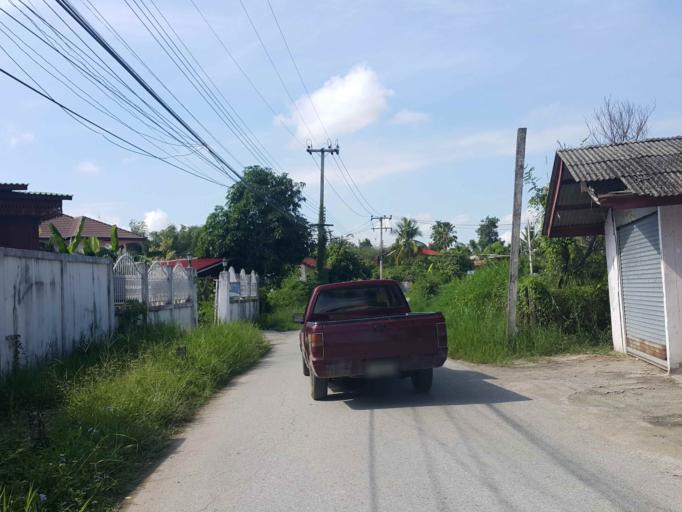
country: TH
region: Chiang Mai
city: San Sai
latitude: 18.8050
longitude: 99.0916
